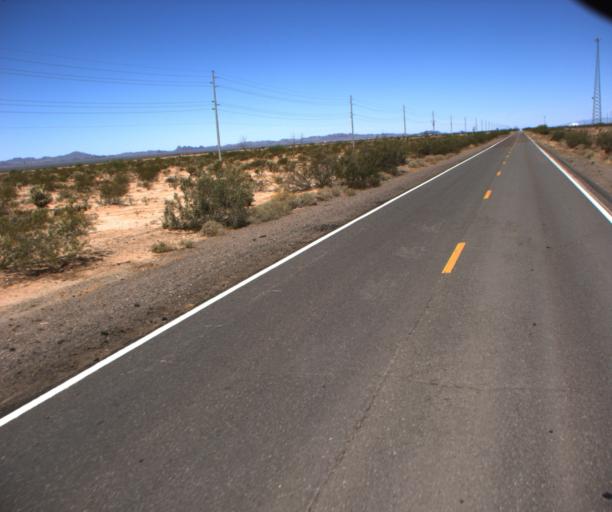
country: US
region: Arizona
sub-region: La Paz County
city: Salome
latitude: 33.8345
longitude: -113.8814
